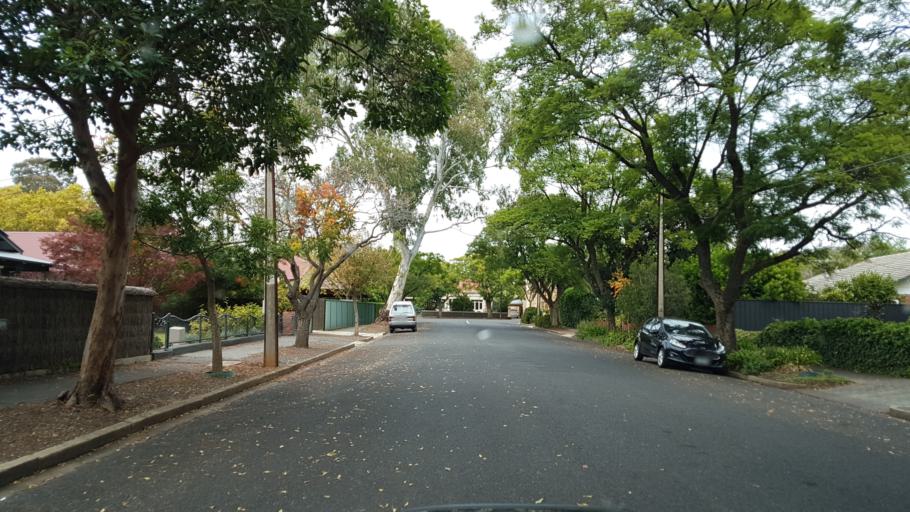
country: AU
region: South Australia
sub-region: Mitcham
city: Hawthorn
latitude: -34.9718
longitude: 138.6055
